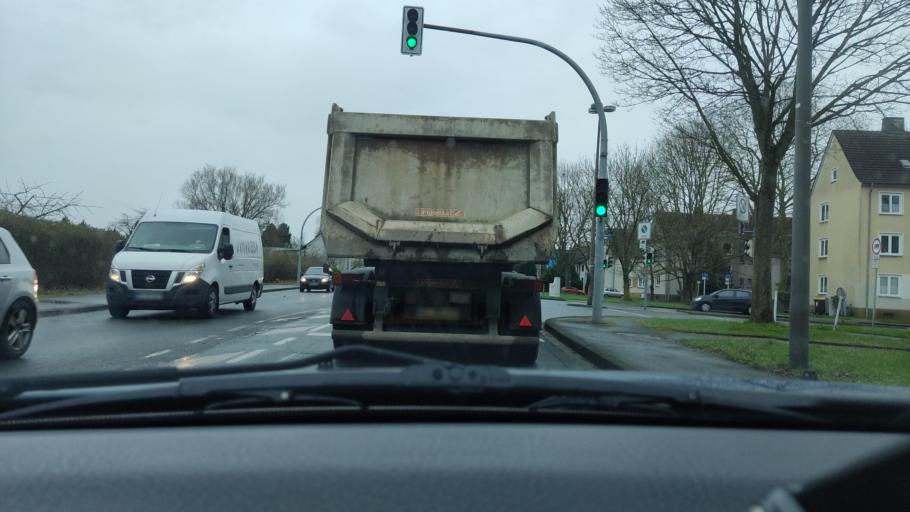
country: DE
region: North Rhine-Westphalia
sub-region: Regierungsbezirk Arnsberg
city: Dortmund
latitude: 51.5587
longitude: 7.4748
